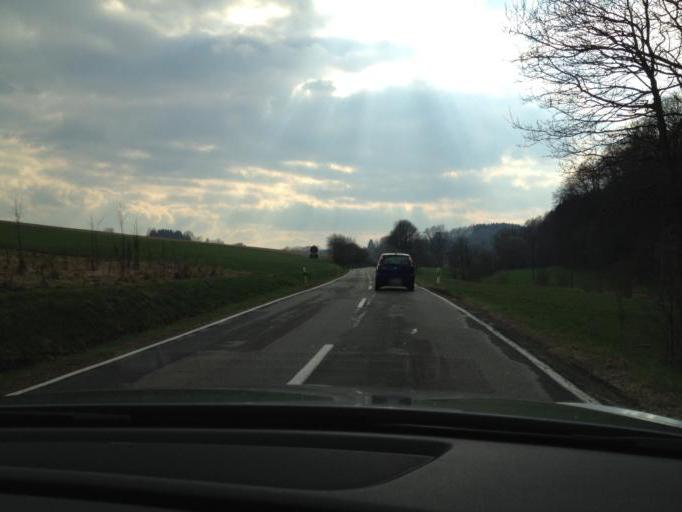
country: DE
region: Saarland
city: Freisen
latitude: 49.4981
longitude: 7.2258
